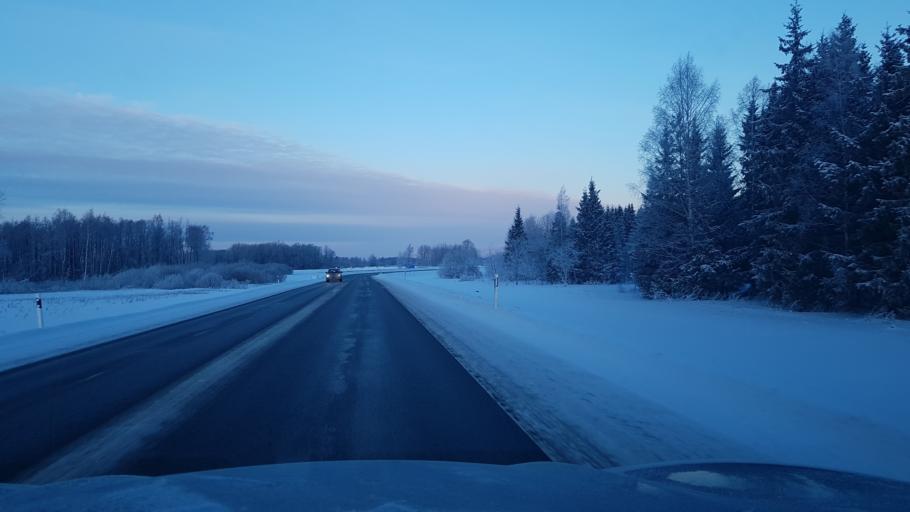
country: EE
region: Ida-Virumaa
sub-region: Narva-Joesuu linn
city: Narva-Joesuu
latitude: 59.3937
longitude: 28.0839
